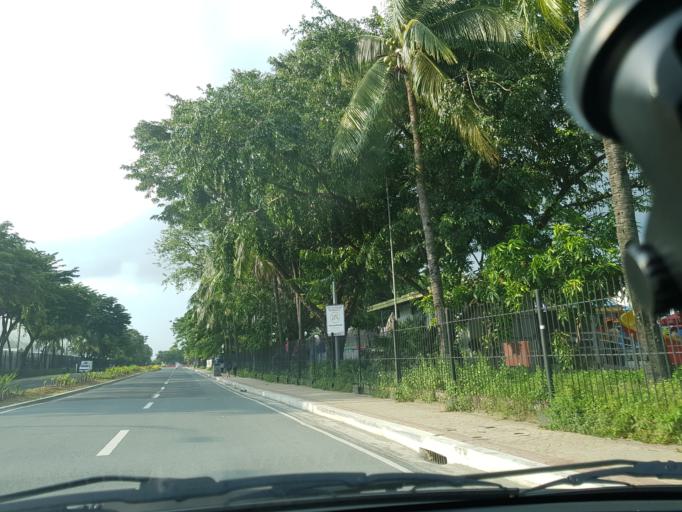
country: PH
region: Metro Manila
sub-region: City of Manila
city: Port Area
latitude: 14.5544
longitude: 120.9852
